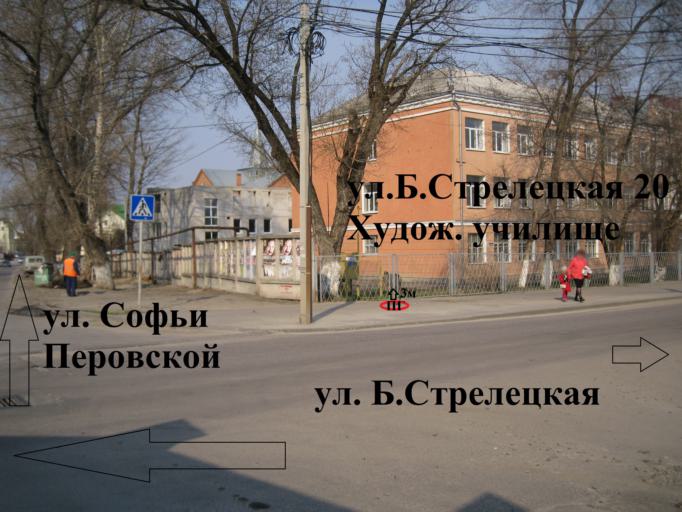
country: RU
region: Voronezj
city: Voronezh
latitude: 51.6518
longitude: 39.2083
